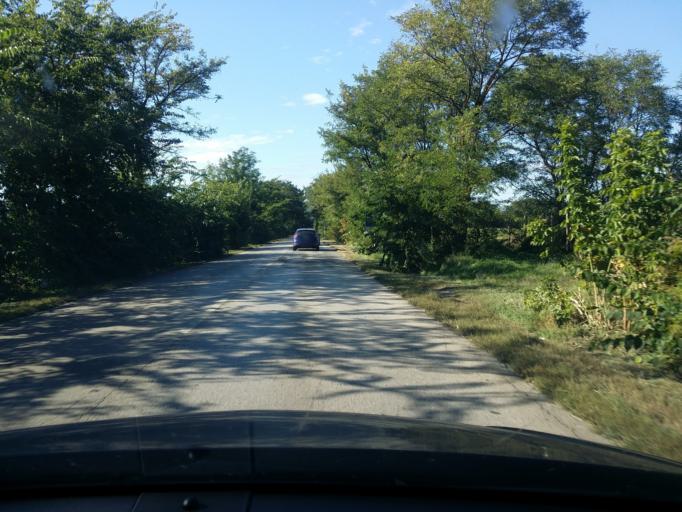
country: HU
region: Pest
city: God
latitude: 47.6863
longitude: 19.1640
